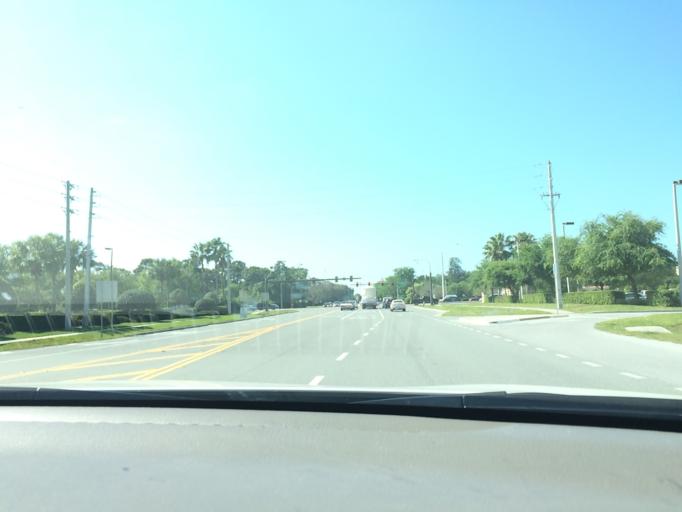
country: US
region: Florida
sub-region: Sarasota County
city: North Sarasota
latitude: 27.3904
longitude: -82.5138
